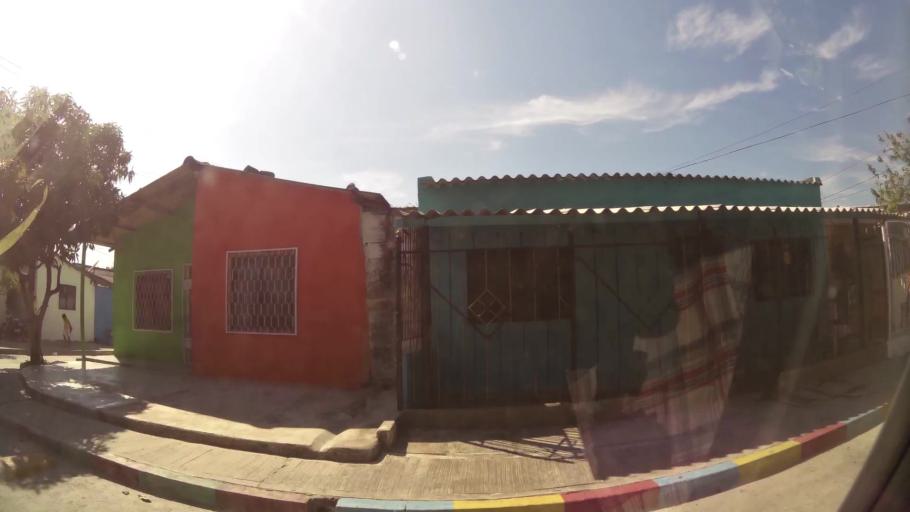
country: CO
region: Atlantico
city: Barranquilla
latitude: 10.9305
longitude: -74.8261
